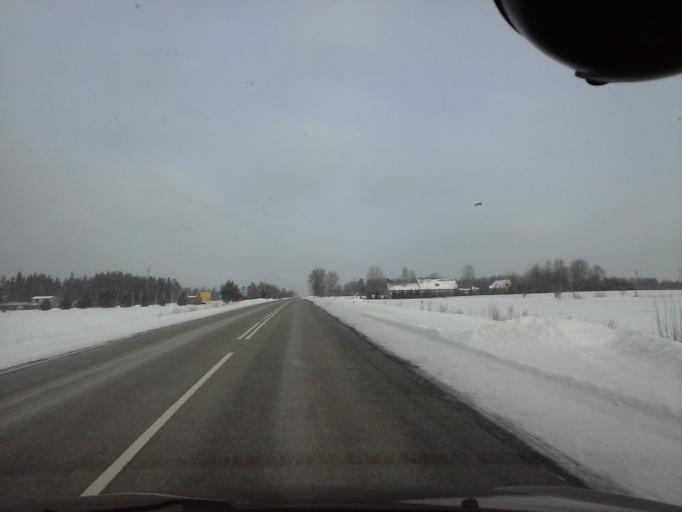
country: EE
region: Paernumaa
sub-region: Saarde vald
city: Kilingi-Nomme
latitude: 58.1651
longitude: 25.0160
